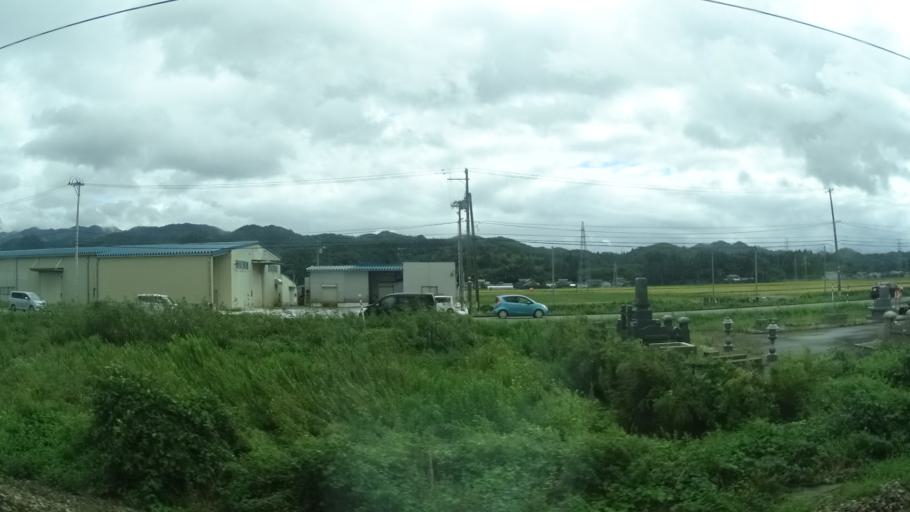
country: JP
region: Niigata
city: Shibata
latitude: 38.0002
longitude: 139.3699
